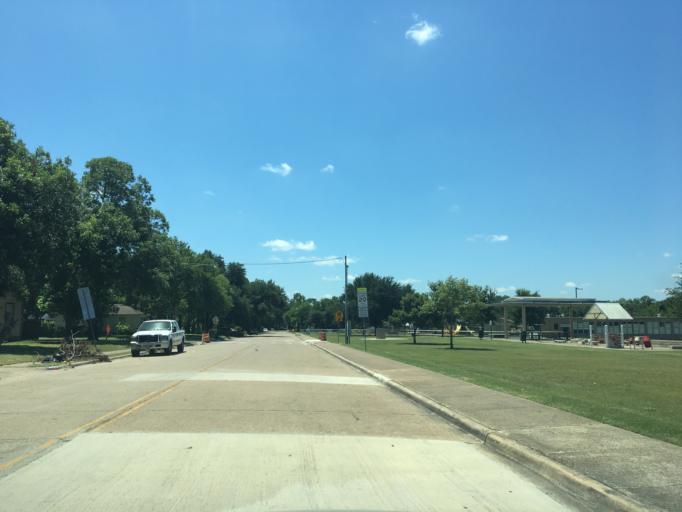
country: US
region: Texas
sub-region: Dallas County
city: Garland
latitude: 32.8472
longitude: -96.6743
